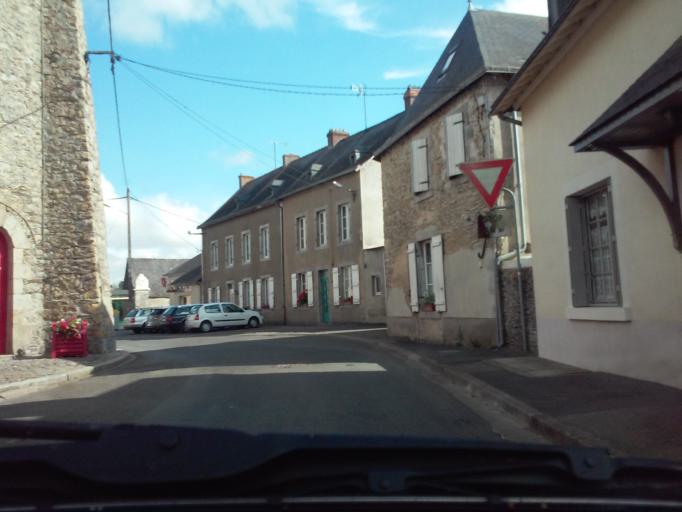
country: FR
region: Pays de la Loire
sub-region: Departement de la Mayenne
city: Argentre
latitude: 48.0575
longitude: -0.6306
